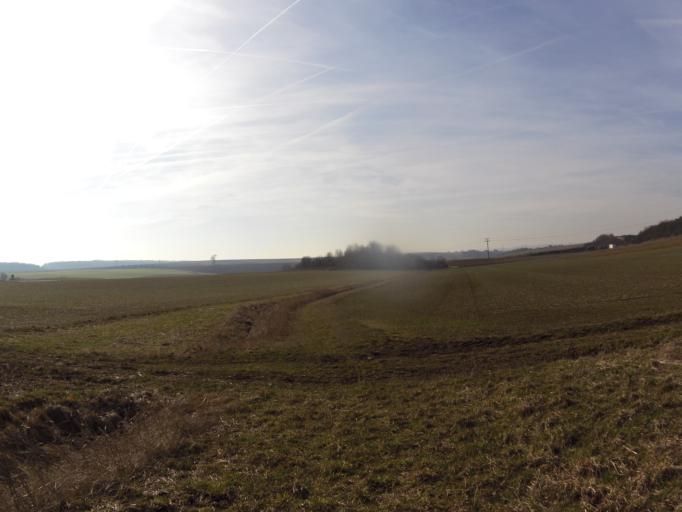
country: DE
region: Bavaria
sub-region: Regierungsbezirk Unterfranken
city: Rottendorf
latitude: 49.8250
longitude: 10.0353
